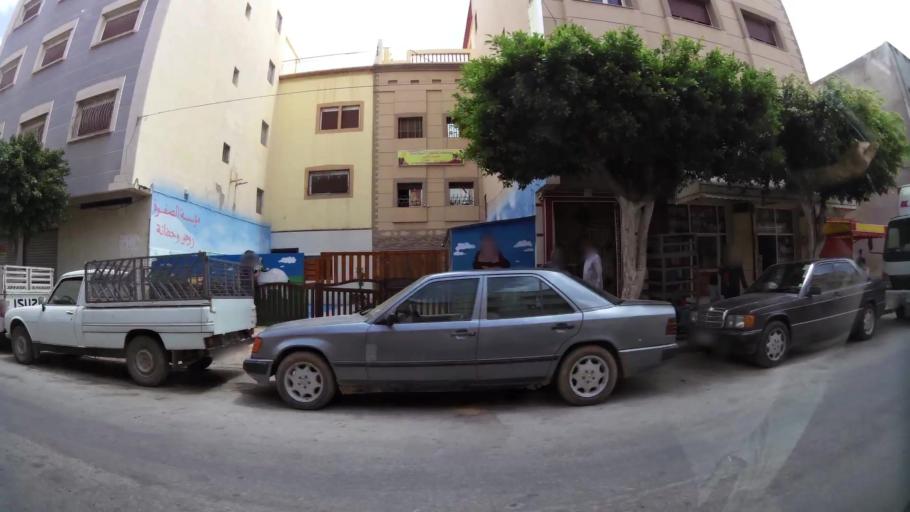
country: MA
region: Oriental
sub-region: Nador
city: Nador
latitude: 35.1700
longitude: -2.9197
